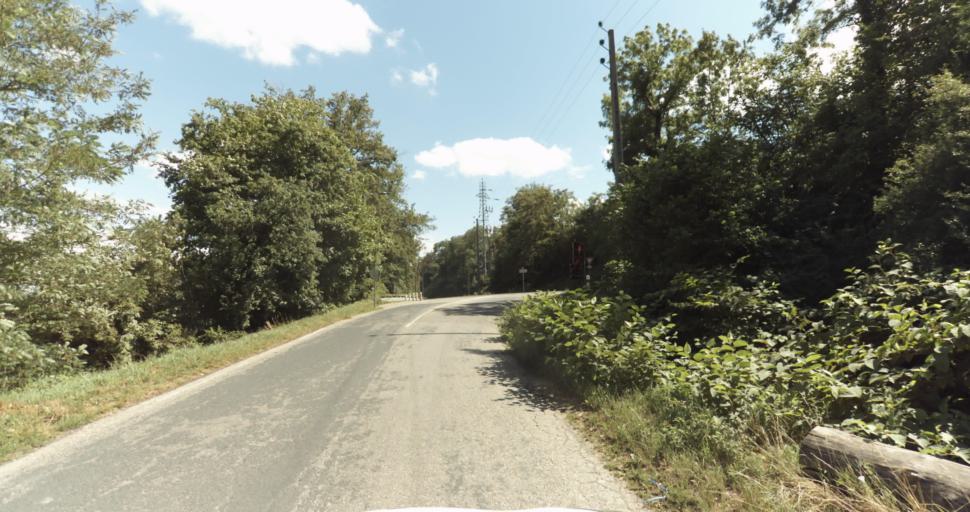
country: FR
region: Rhone-Alpes
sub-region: Departement du Rhone
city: Francheville
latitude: 45.7263
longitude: 4.7721
